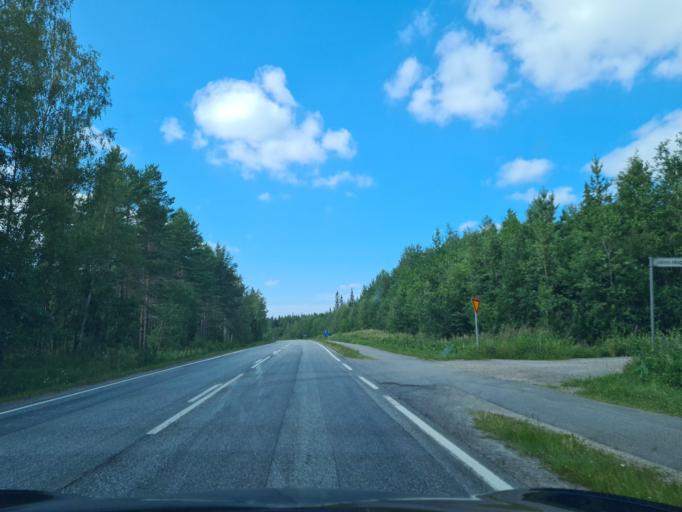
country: FI
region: Ostrobothnia
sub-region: Vaasa
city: Replot
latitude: 63.2022
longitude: 21.5292
